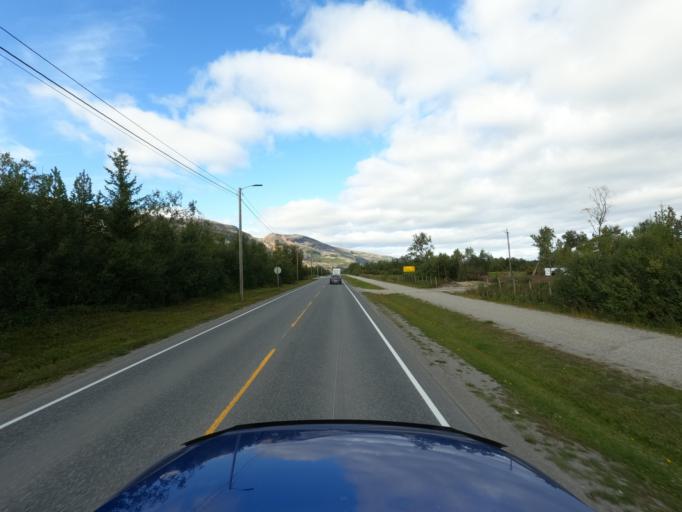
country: NO
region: Finnmark Fylke
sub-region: Porsanger
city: Lakselv
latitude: 70.0548
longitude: 24.9394
